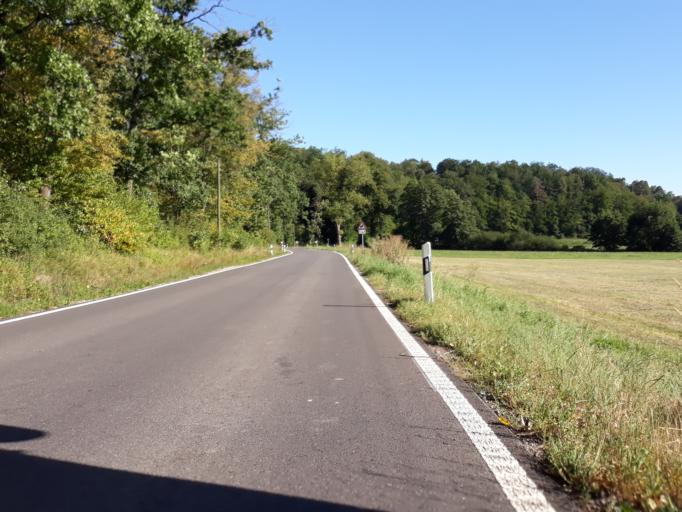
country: DE
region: Baden-Wuerttemberg
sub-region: Regierungsbezirk Stuttgart
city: Ehningen
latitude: 48.6575
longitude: 8.9657
